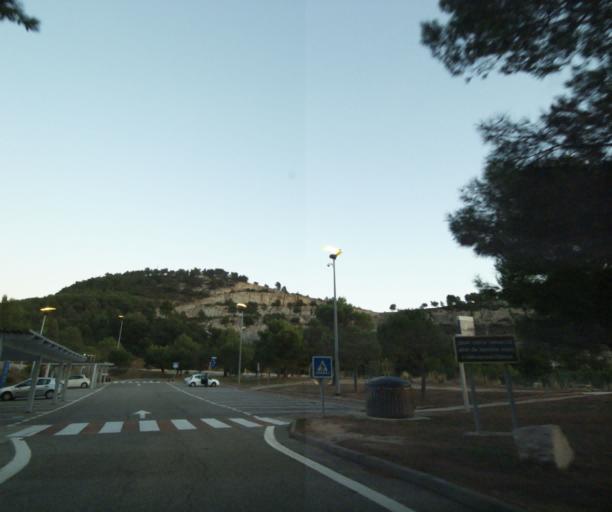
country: FR
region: Provence-Alpes-Cote d'Azur
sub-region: Departement des Bouches-du-Rhone
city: Roquefort-la-Bedoule
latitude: 43.2374
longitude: 5.5888
